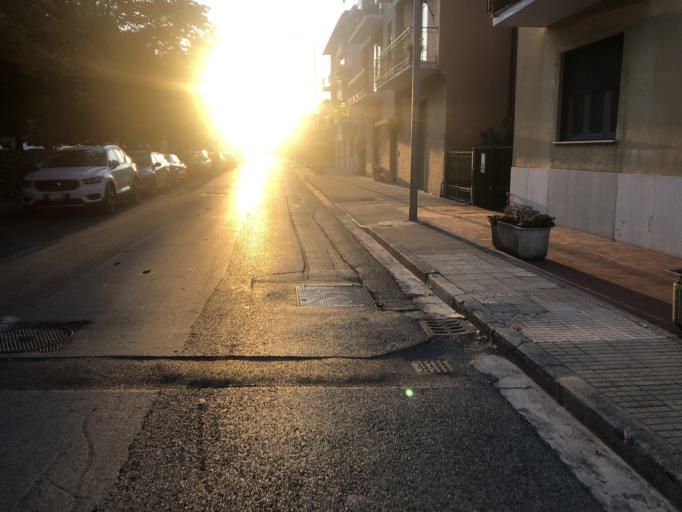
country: IT
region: Tuscany
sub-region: Province of Pisa
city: Pisa
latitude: 43.7271
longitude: 10.4098
